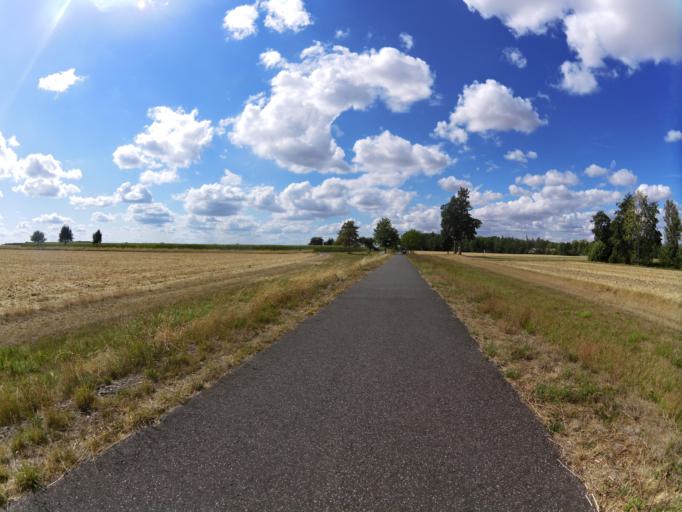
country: DE
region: Bavaria
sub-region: Regierungsbezirk Unterfranken
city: Sonderhofen
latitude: 49.5680
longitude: 10.0289
